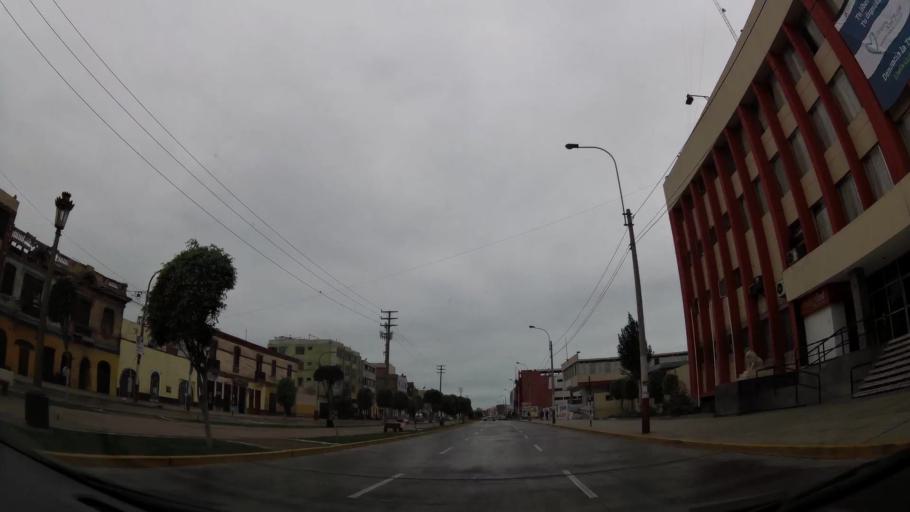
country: PE
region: Callao
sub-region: Callao
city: Callao
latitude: -12.0568
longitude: -77.1426
